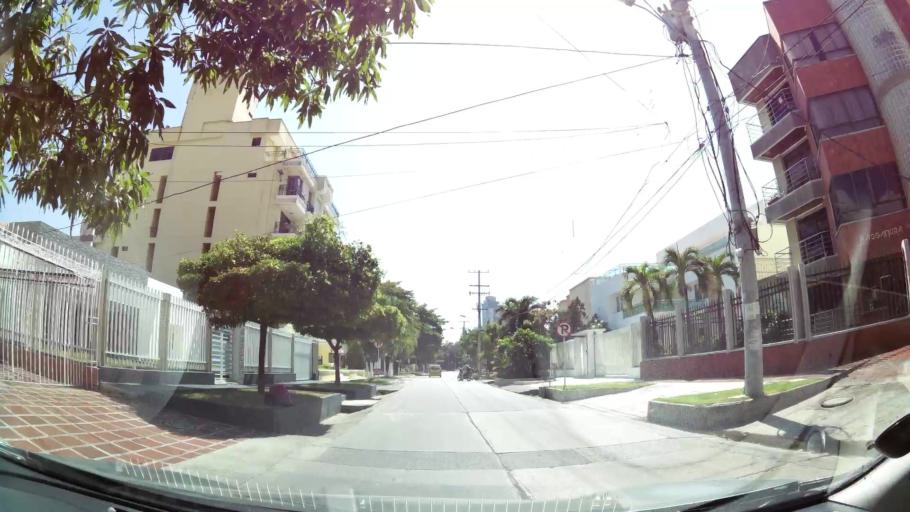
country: CO
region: Atlantico
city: Barranquilla
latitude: 11.0146
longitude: -74.8171
